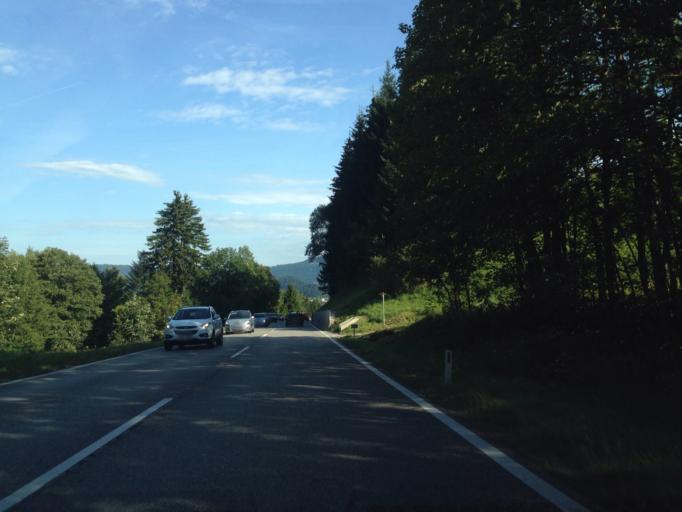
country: AT
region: Tyrol
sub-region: Politischer Bezirk Reutte
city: Breitenwang
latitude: 47.4704
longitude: 10.7256
